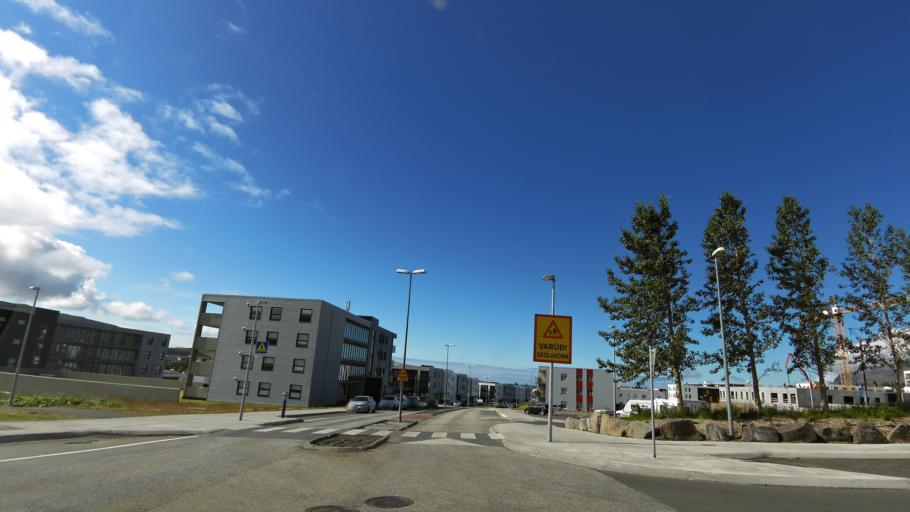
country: IS
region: Capital Region
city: Mosfellsbaer
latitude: 64.1673
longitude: -21.6646
